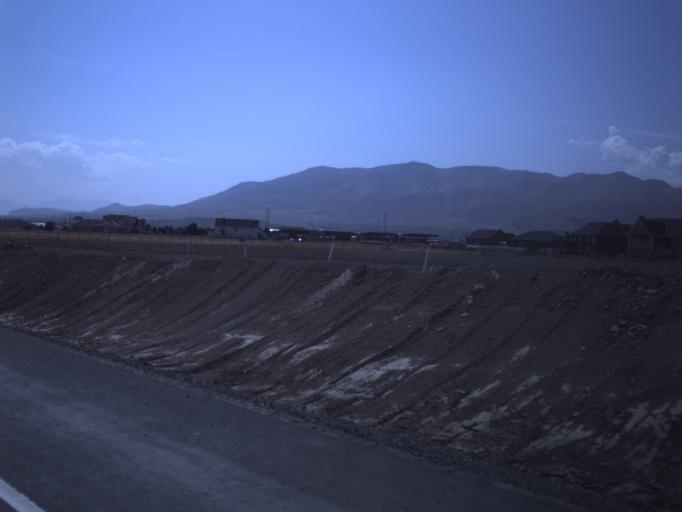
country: US
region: Utah
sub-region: Utah County
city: Saratoga Springs
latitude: 40.3747
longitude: -111.9228
